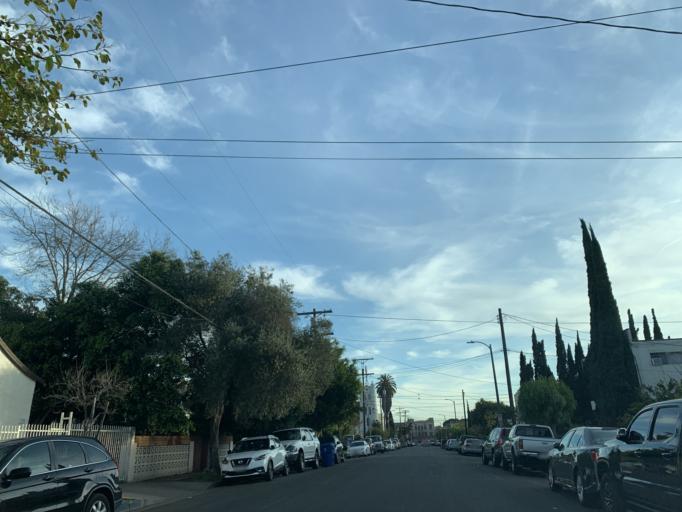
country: US
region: California
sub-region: Los Angeles County
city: Silver Lake
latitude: 34.0503
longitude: -118.2969
